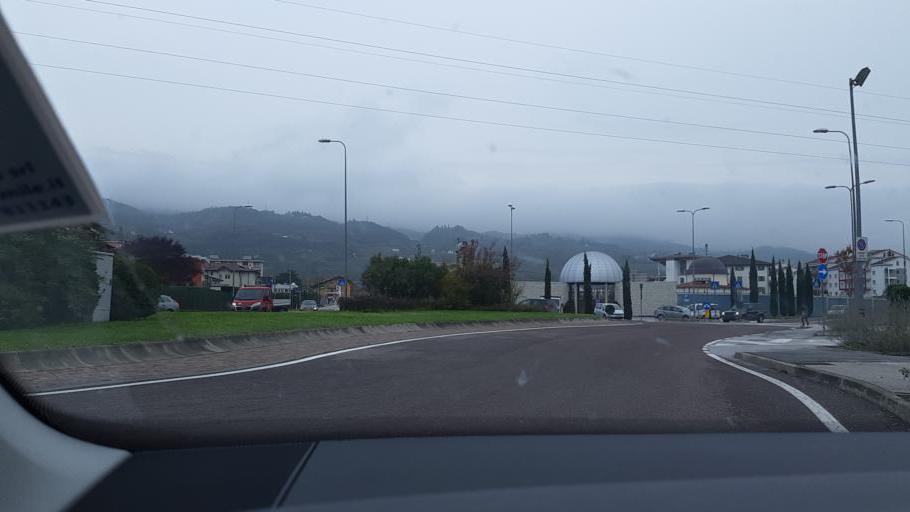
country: IT
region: Trentino-Alto Adige
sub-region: Provincia di Trento
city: Lavis
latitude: 46.1421
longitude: 11.1042
